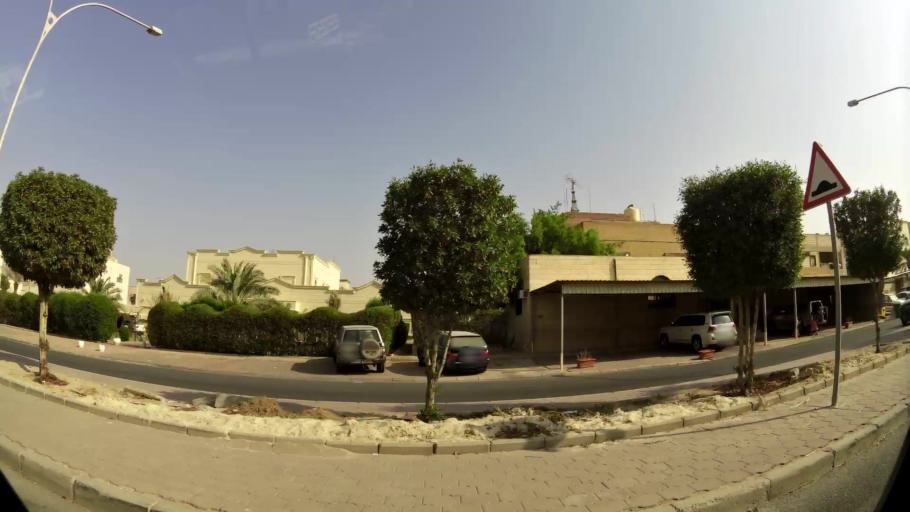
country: KW
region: Muhafazat al Jahra'
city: Al Jahra'
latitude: 29.3418
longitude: 47.7032
